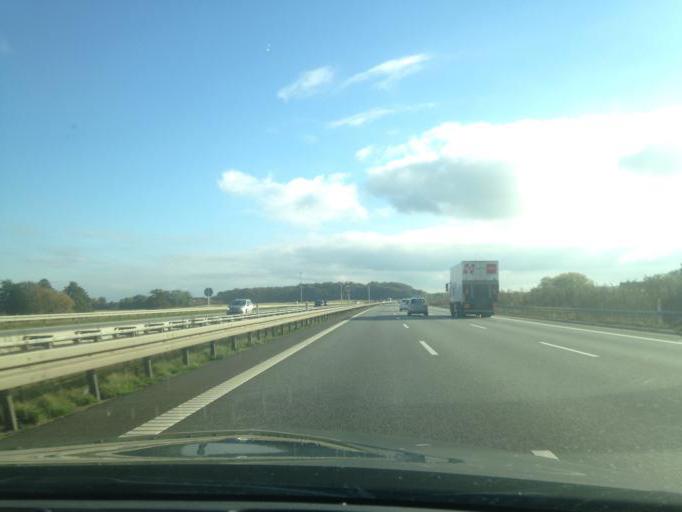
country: DK
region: South Denmark
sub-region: Vejle Kommune
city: Borkop
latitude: 55.6165
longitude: 9.5786
